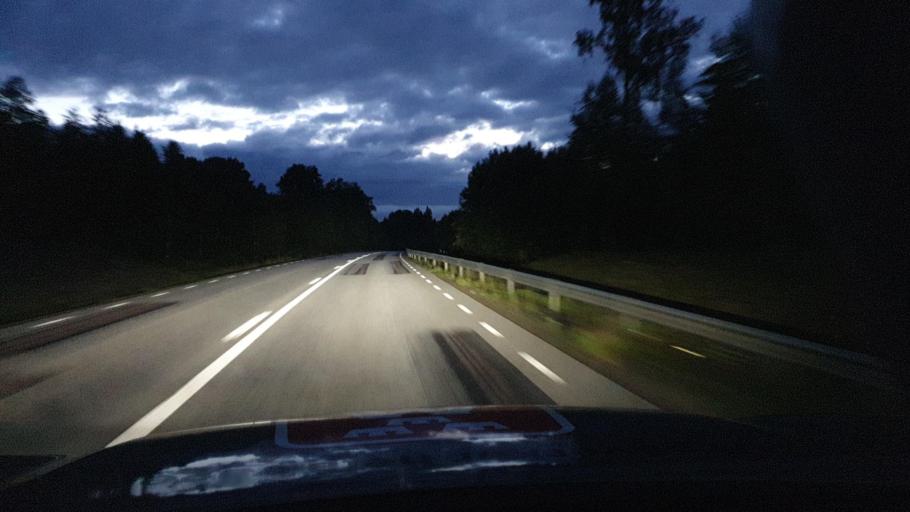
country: SE
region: OErebro
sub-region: Karlskoga Kommun
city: Karlskoga
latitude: 59.4488
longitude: 14.5096
